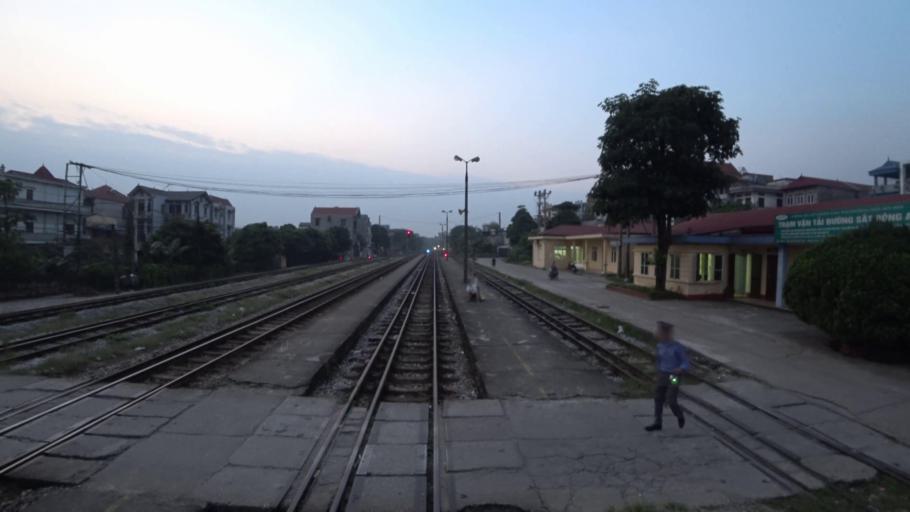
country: VN
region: Ha Noi
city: Soc Son
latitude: 21.2403
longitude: 105.8614
